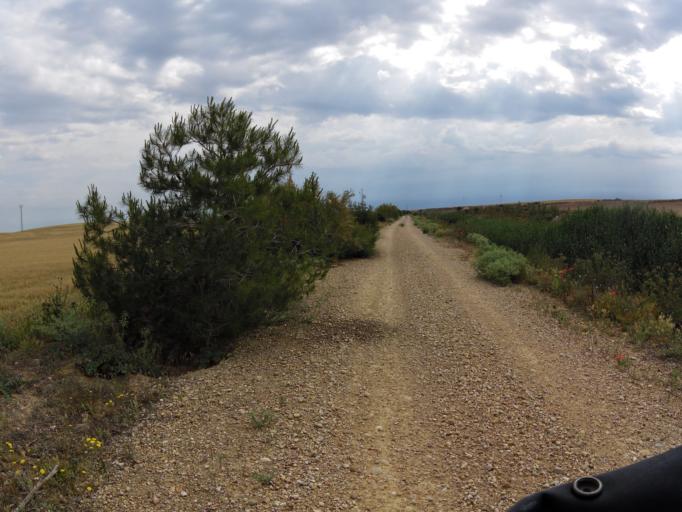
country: ES
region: Castille-La Mancha
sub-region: Provincia de Albacete
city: Albacete
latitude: 39.0384
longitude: -1.7869
